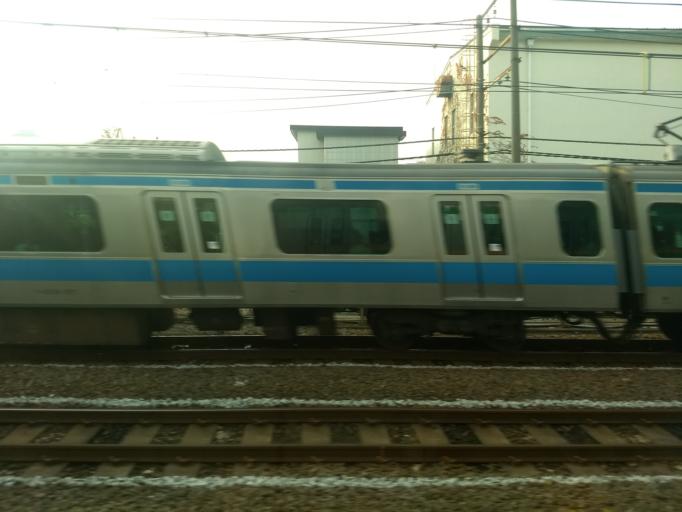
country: JP
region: Tokyo
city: Tokyo
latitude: 35.6124
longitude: 139.7357
